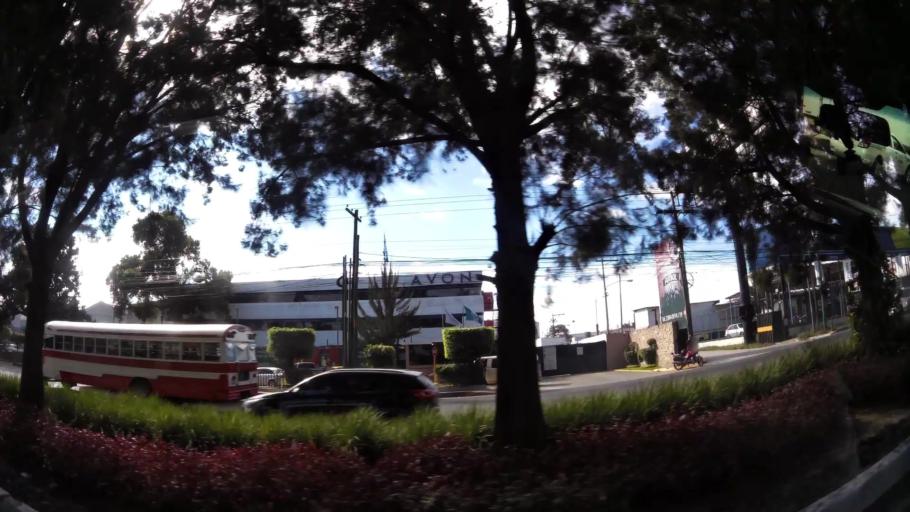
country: GT
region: Guatemala
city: Mixco
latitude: 14.6340
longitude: -90.5773
